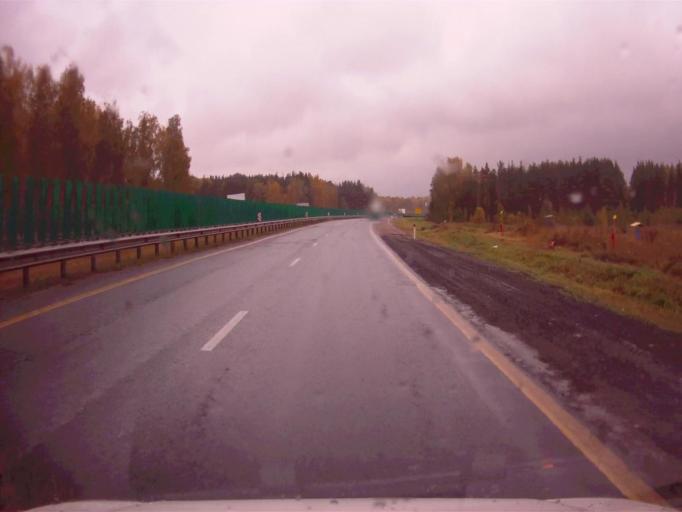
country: RU
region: Chelyabinsk
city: Dolgoderevenskoye
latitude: 55.3372
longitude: 61.3090
